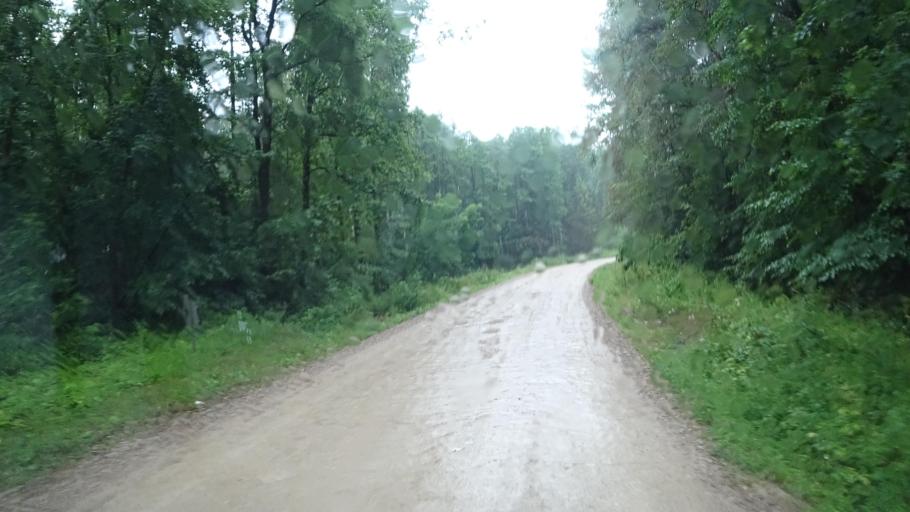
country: LV
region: Lecava
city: Iecava
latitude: 56.6600
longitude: 24.1738
